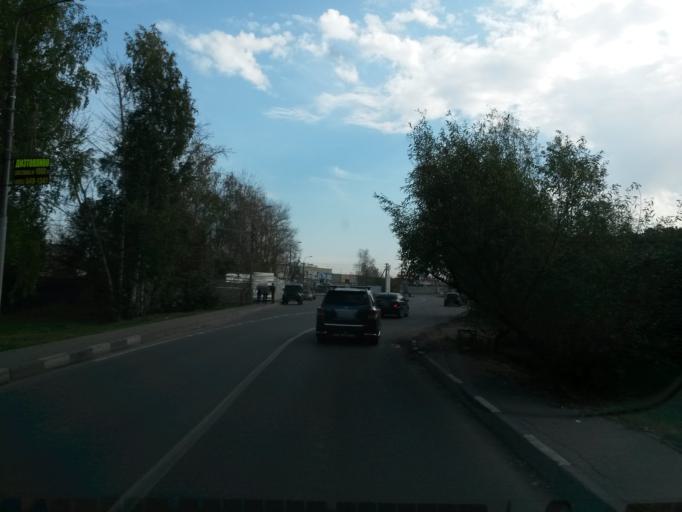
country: RU
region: Moskovskaya
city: Mosrentgen
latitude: 55.6154
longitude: 37.4778
